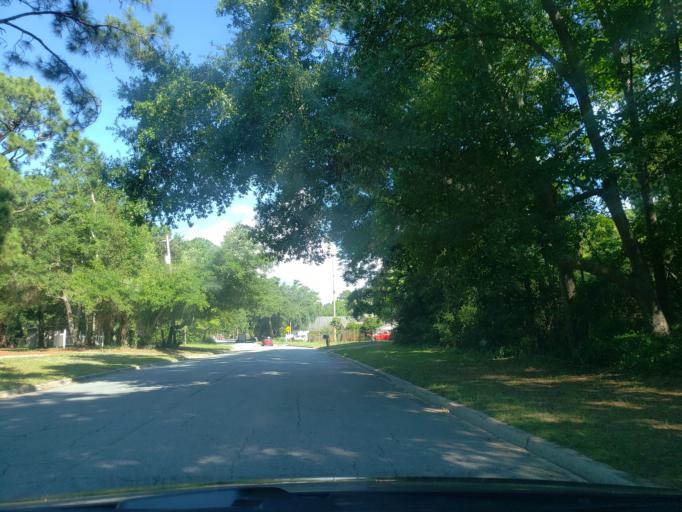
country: US
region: Georgia
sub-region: Chatham County
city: Montgomery
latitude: 31.9874
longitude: -81.1635
